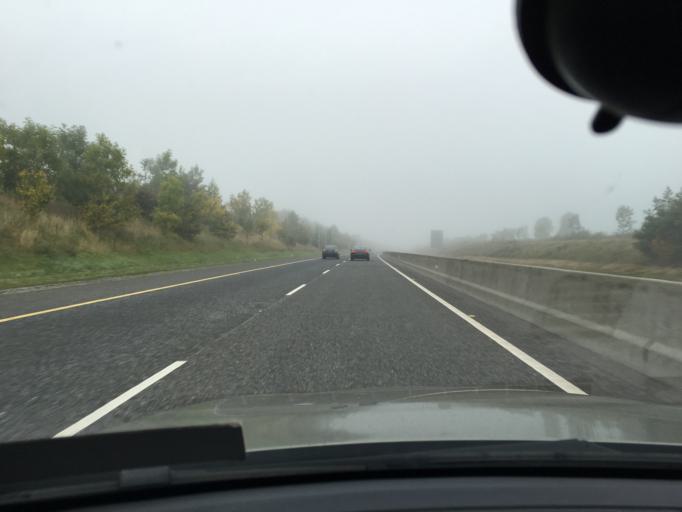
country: IE
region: Leinster
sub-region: An Iarmhi
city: Moate
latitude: 53.3950
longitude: -7.8054
